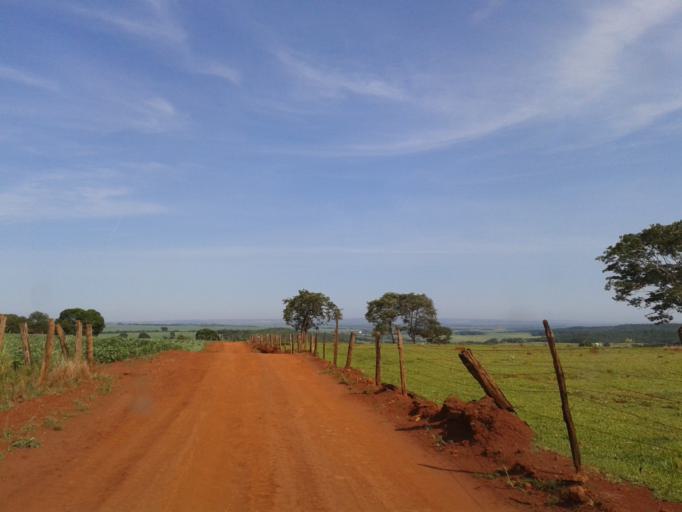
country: BR
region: Minas Gerais
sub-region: Centralina
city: Centralina
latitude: -18.7117
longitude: -49.2030
